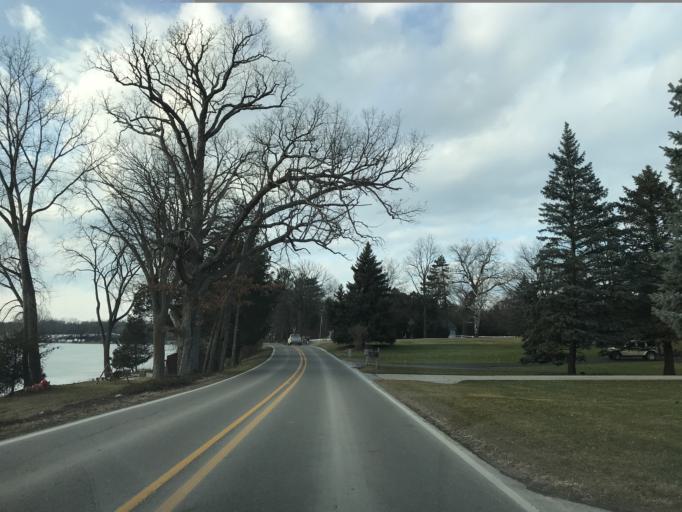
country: US
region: Michigan
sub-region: Livingston County
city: Whitmore Lake
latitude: 42.4693
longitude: -83.7185
